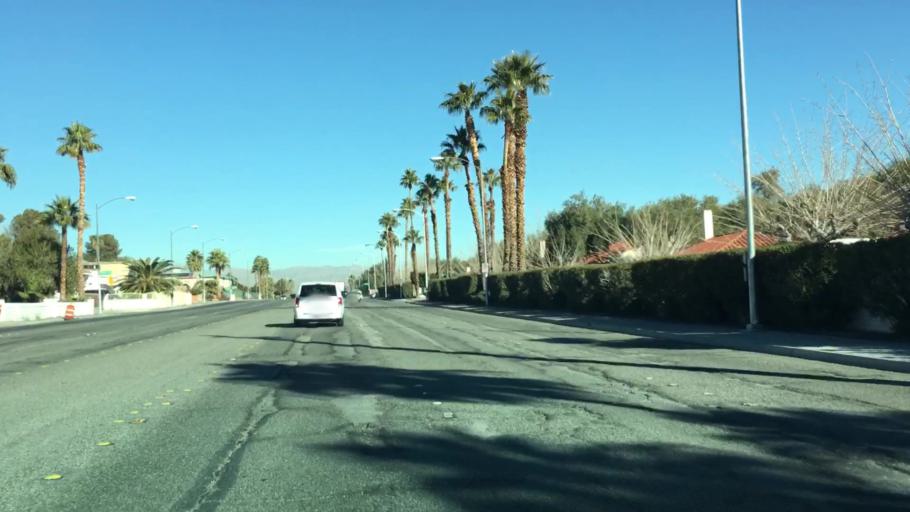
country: US
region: Nevada
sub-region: Clark County
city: Winchester
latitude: 36.1241
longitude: -115.1187
